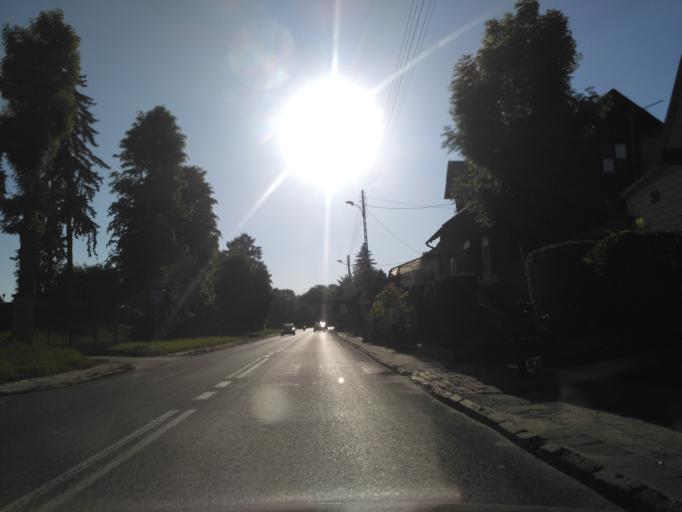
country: PL
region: Lublin Voivodeship
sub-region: Powiat lubelski
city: Bychawa
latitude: 51.0172
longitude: 22.5273
